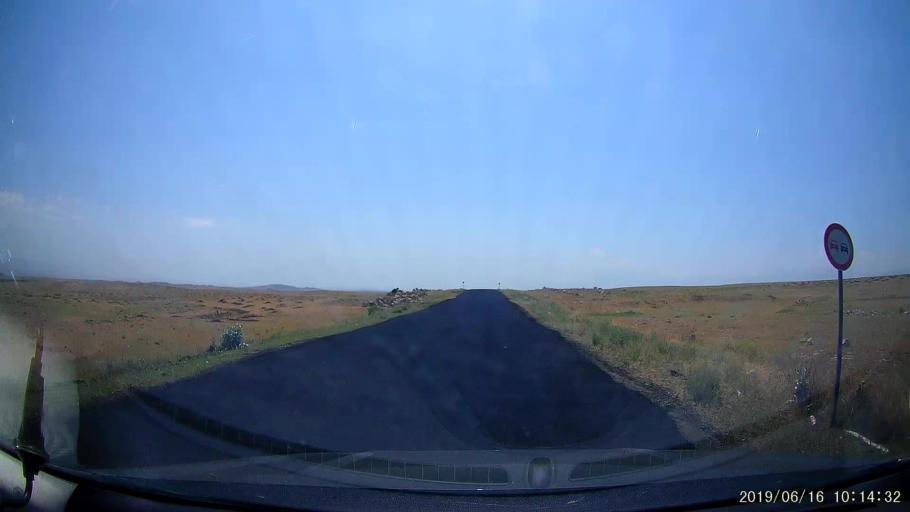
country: TR
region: Igdir
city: Tuzluca
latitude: 40.1840
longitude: 43.6647
